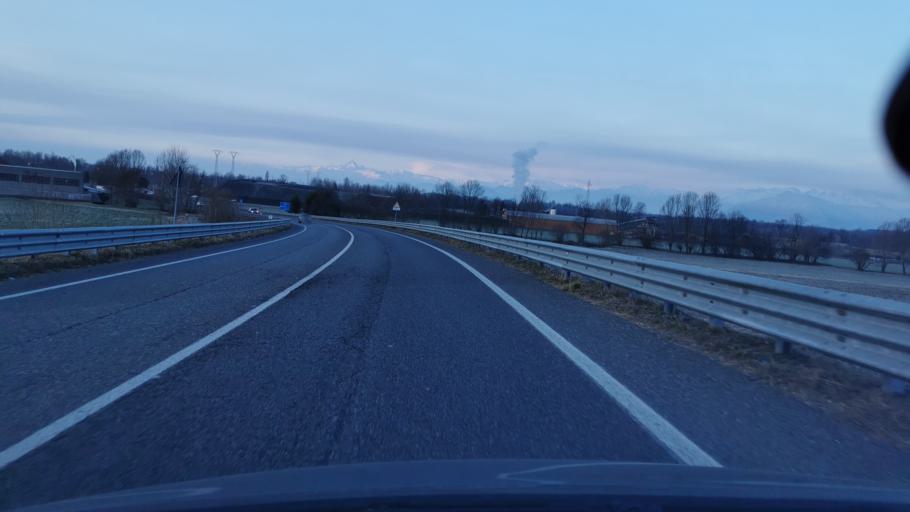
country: IT
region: Piedmont
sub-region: Provincia di Torino
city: Borgaro Torinese
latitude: 45.1573
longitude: 7.6462
